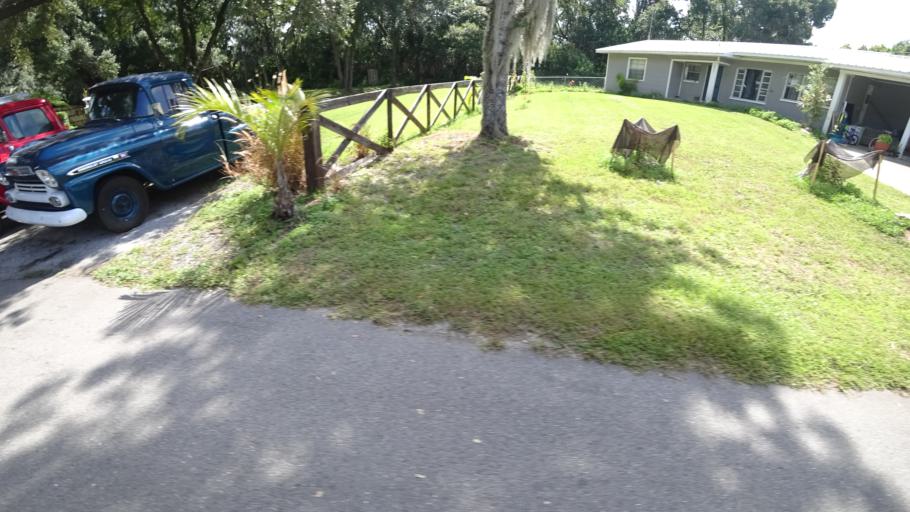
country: US
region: Florida
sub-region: Manatee County
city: Samoset
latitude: 27.4746
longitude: -82.4858
